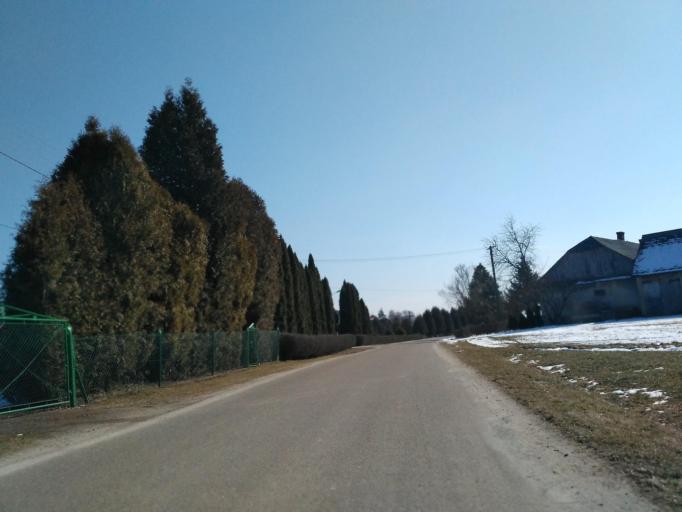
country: PL
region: Subcarpathian Voivodeship
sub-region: Powiat brzozowski
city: Jasienica Rosielna
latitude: 49.7709
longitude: 21.9177
